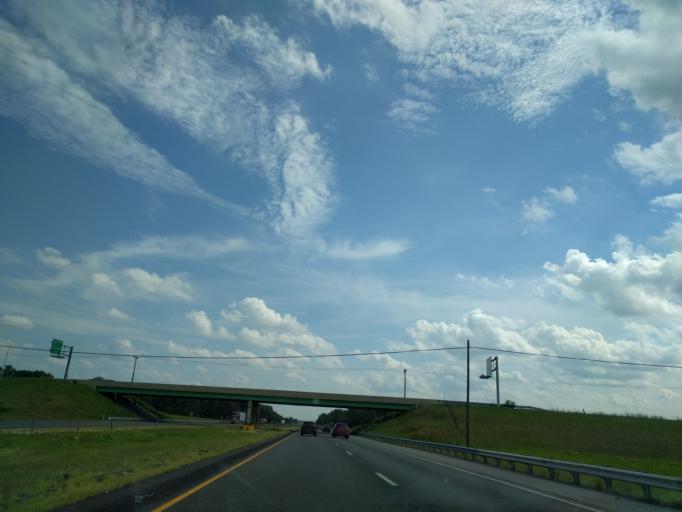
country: US
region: Indiana
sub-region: Jasper County
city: Rensselaer
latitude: 40.9417
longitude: -87.2212
